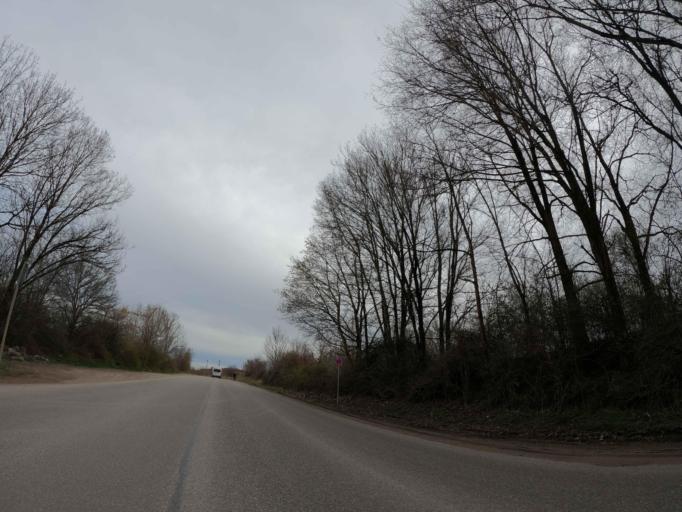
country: DE
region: Bavaria
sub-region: Upper Bavaria
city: Oberhaching
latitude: 48.0306
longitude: 11.6106
